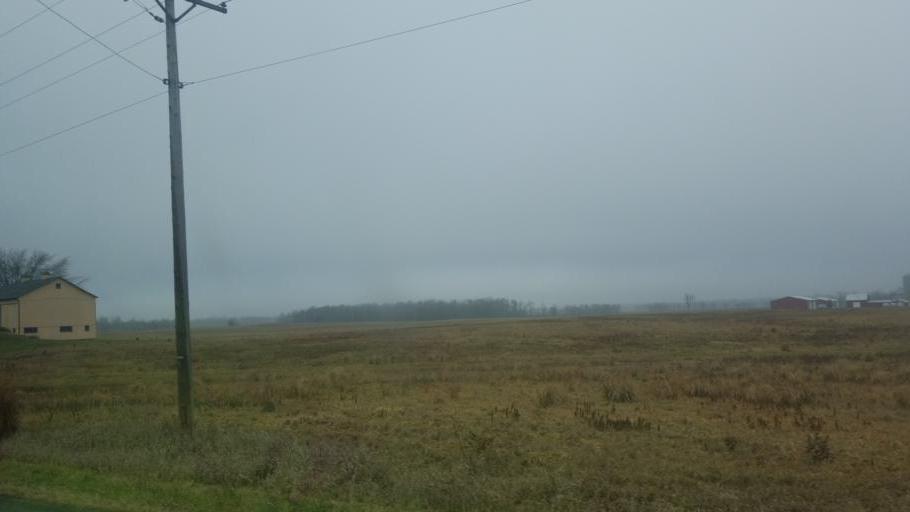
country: US
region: Ohio
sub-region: Champaign County
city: North Lewisburg
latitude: 40.2441
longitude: -83.5717
